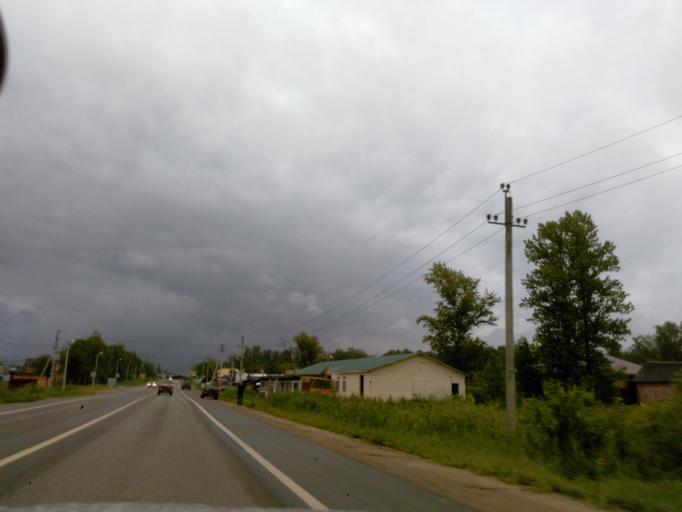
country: RU
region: Moskovskaya
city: Povarovo
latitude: 56.0210
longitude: 37.0045
